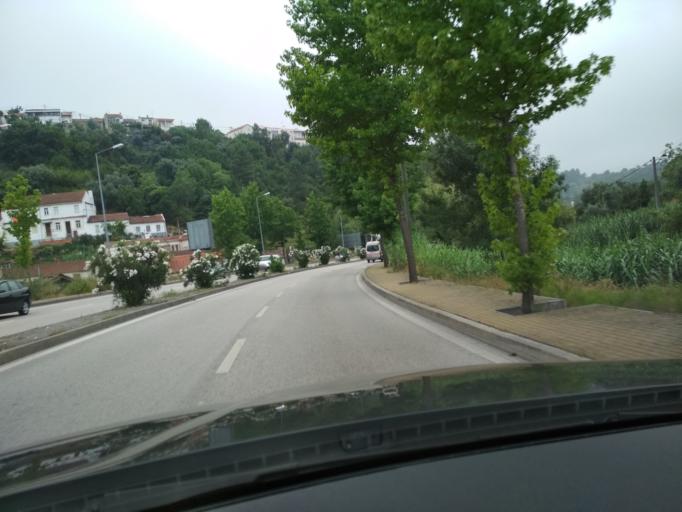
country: PT
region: Coimbra
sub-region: Coimbra
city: Coimbra
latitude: 40.2183
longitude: -8.4267
